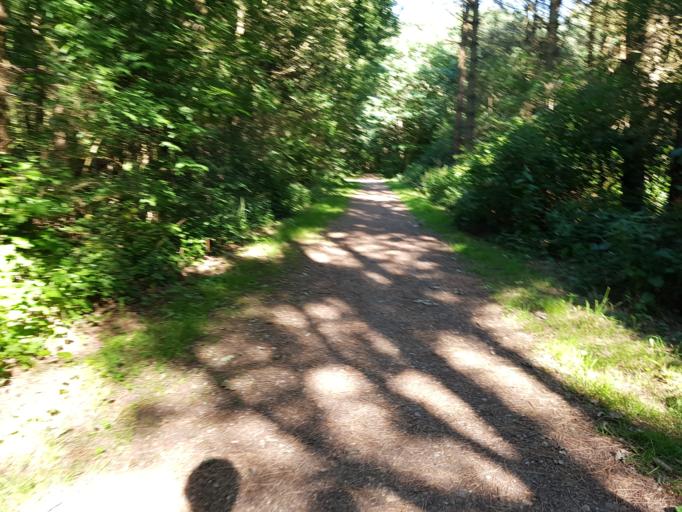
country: DK
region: South Denmark
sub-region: Esbjerg Kommune
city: Esbjerg
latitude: 55.4863
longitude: 8.5150
